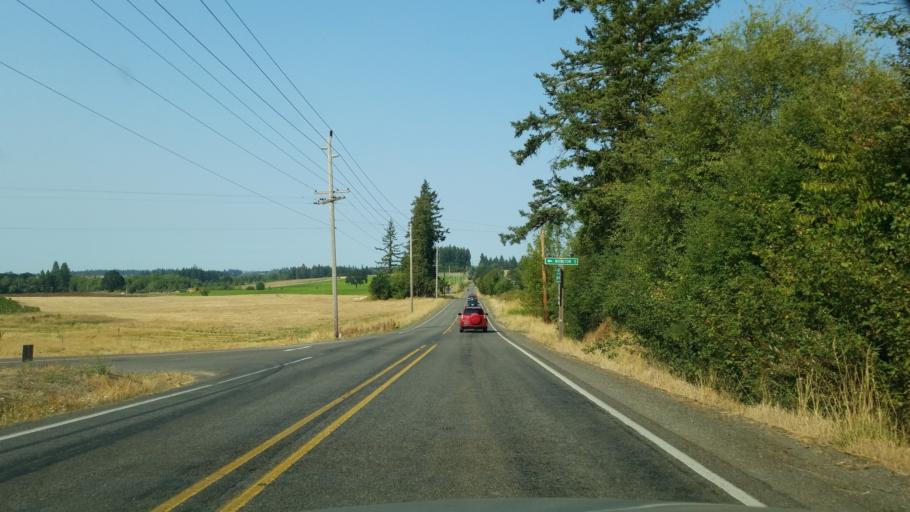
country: US
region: Oregon
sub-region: Clackamas County
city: Molalla
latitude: 45.0997
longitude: -122.6508
